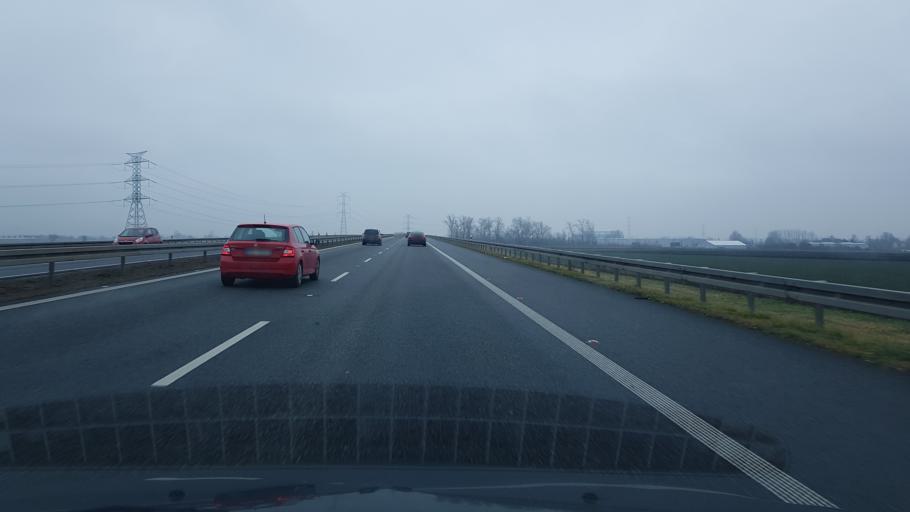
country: PL
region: Lower Silesian Voivodeship
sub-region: Powiat wroclawski
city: Zorawina
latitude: 50.9949
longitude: 17.0470
